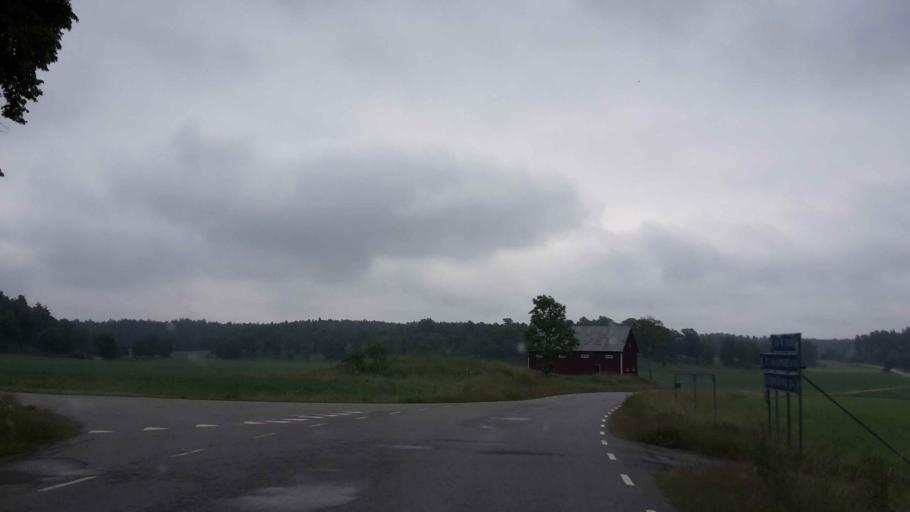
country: SE
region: OEstergoetland
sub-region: Valdemarsviks Kommun
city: Valdemarsvik
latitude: 58.3443
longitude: 16.6076
